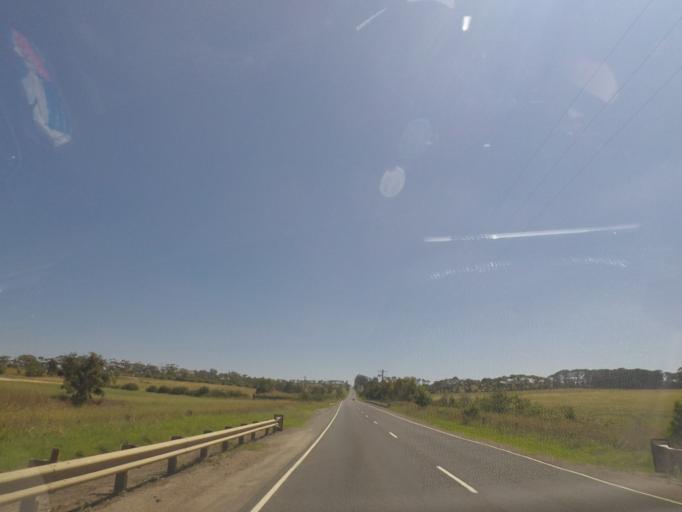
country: AU
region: Victoria
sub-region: Hume
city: Greenvale
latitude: -37.6044
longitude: 144.8408
